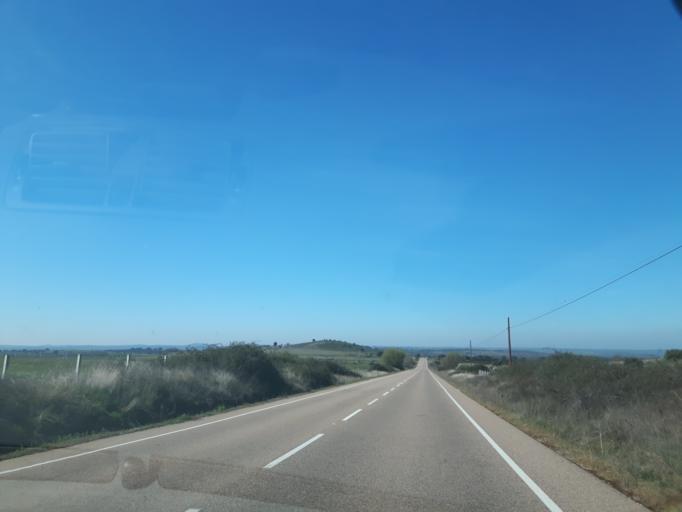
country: ES
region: Castille and Leon
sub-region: Provincia de Salamanca
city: Guadramiro
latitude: 41.0056
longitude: -6.5033
